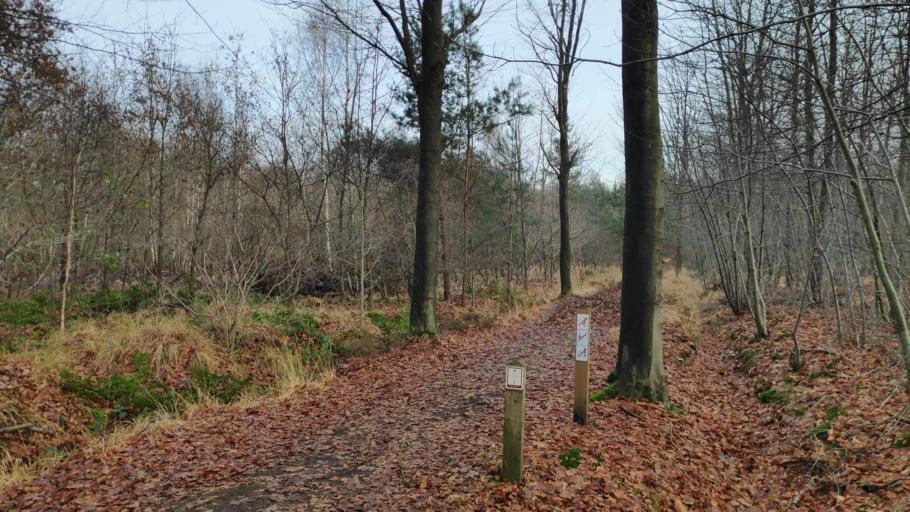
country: BE
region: Flanders
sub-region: Provincie Oost-Vlaanderen
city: Knesselare
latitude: 51.1530
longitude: 3.4411
